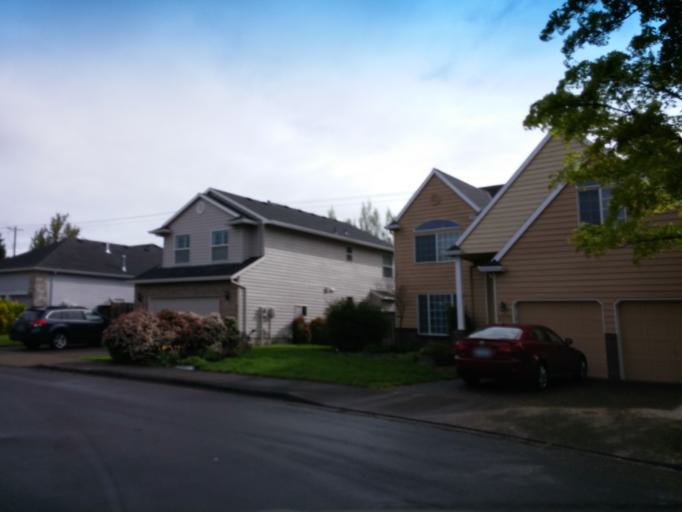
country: US
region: Oregon
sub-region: Washington County
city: Oak Hills
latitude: 45.5368
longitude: -122.8412
